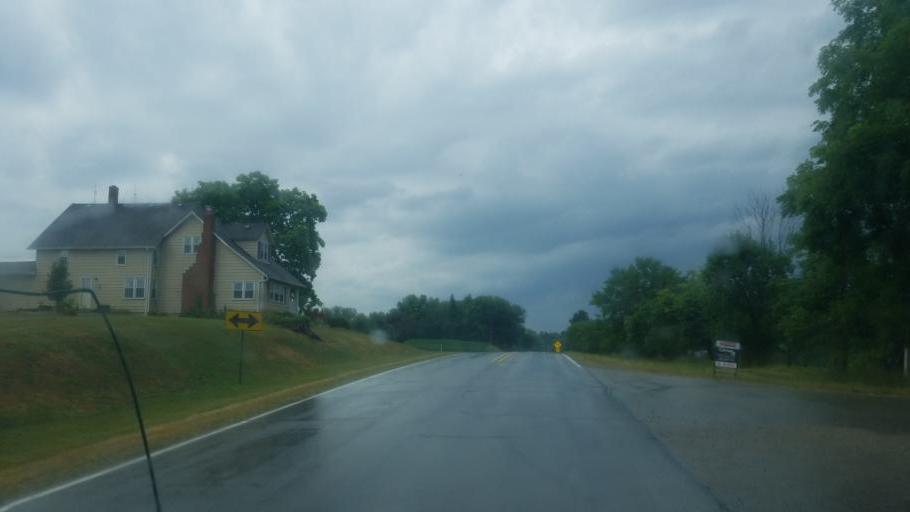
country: US
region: Indiana
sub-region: Steuben County
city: Hamilton
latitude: 41.5130
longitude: -84.8729
